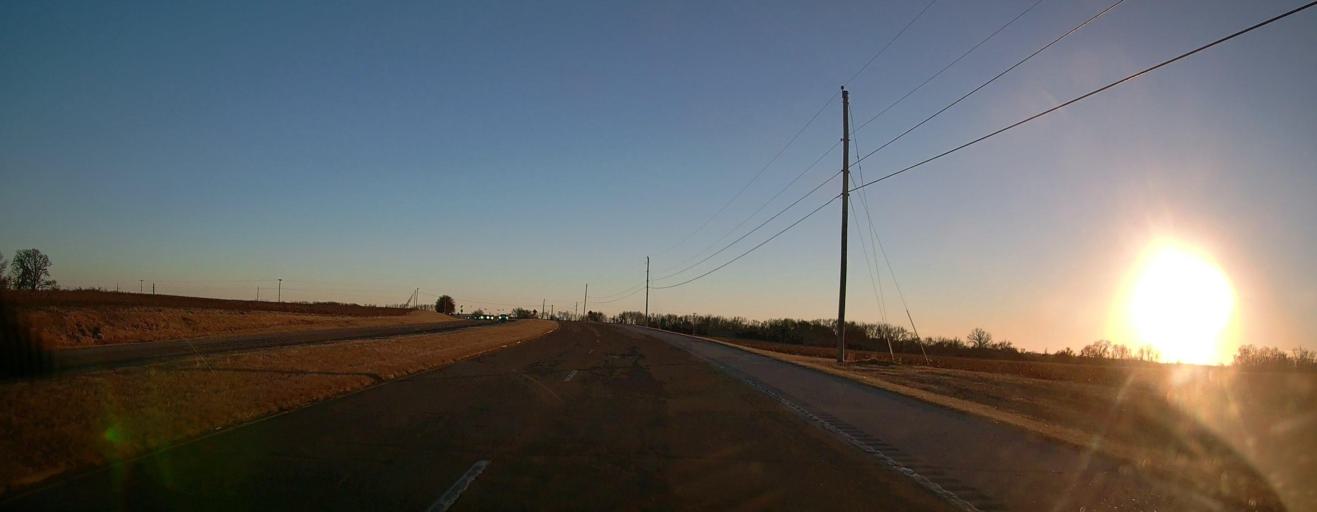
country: US
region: Tennessee
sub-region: Shelby County
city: Millington
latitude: 35.3095
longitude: -89.8814
